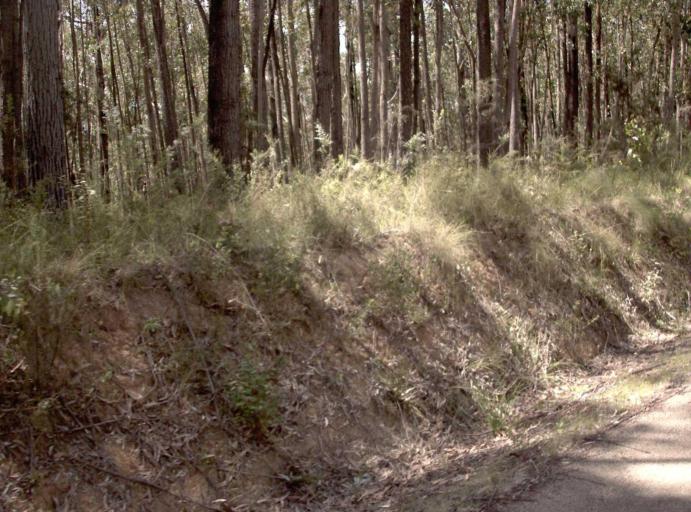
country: AU
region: New South Wales
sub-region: Bombala
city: Bombala
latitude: -37.5656
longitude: 149.3261
